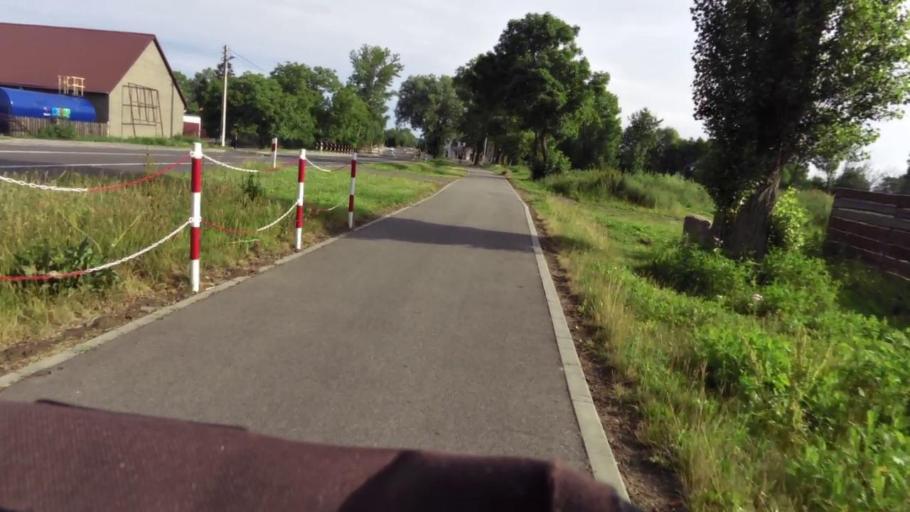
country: PL
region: West Pomeranian Voivodeship
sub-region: Powiat kamienski
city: Kamien Pomorski
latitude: 53.9965
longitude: 14.8175
